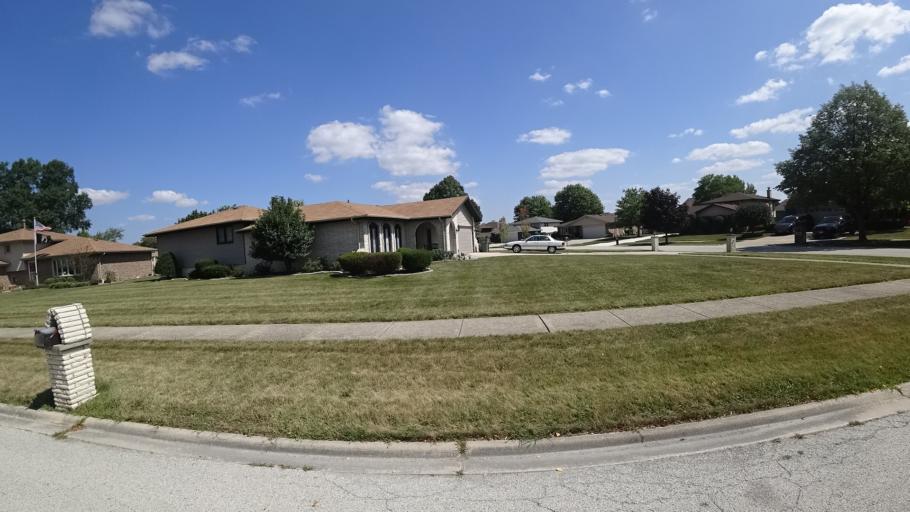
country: US
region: Illinois
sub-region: Cook County
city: Orland Park
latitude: 41.6325
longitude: -87.8355
